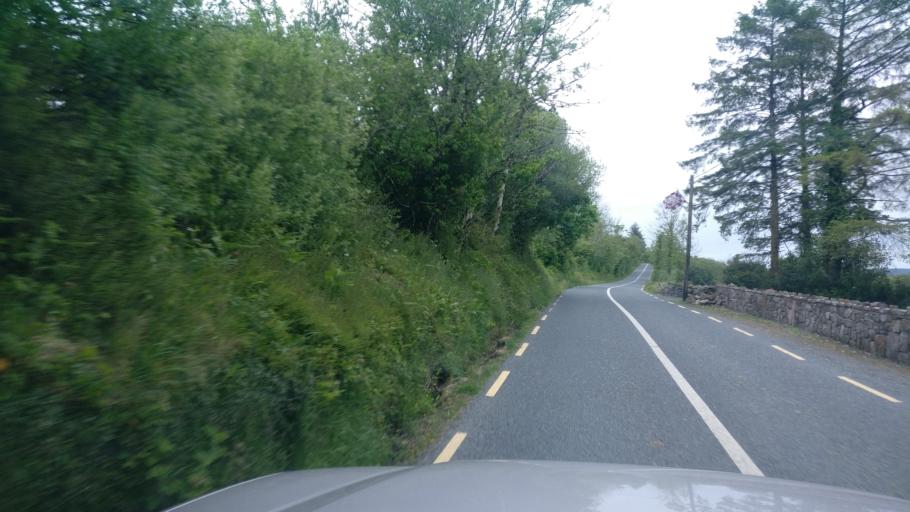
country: IE
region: Connaught
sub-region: County Galway
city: Loughrea
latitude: 53.0616
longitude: -8.6310
